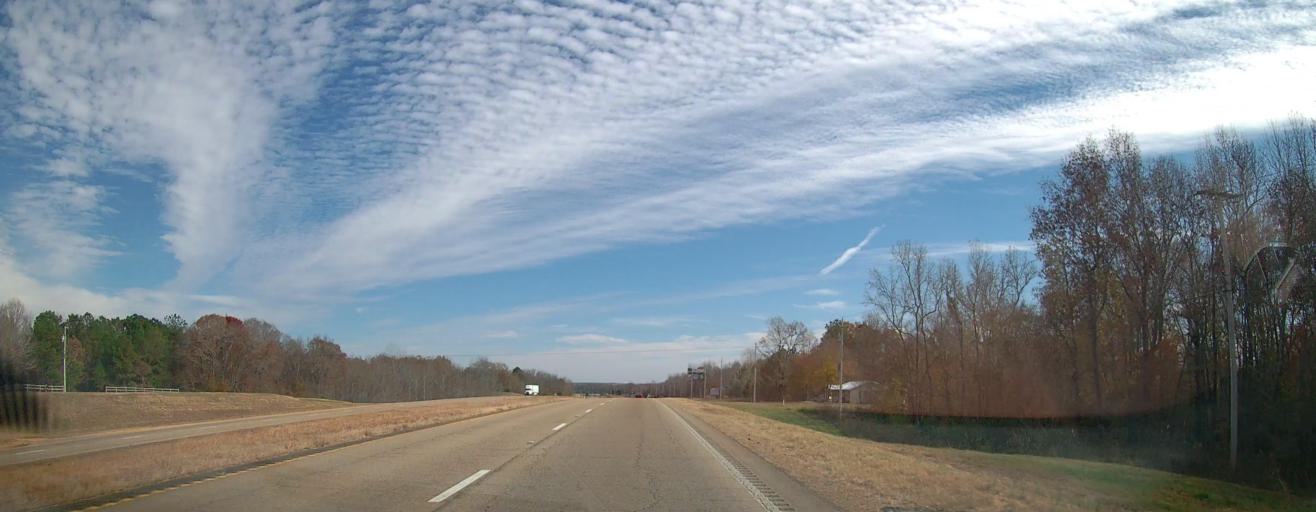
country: US
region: Mississippi
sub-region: Alcorn County
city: Corinth
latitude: 34.9323
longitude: -88.6463
